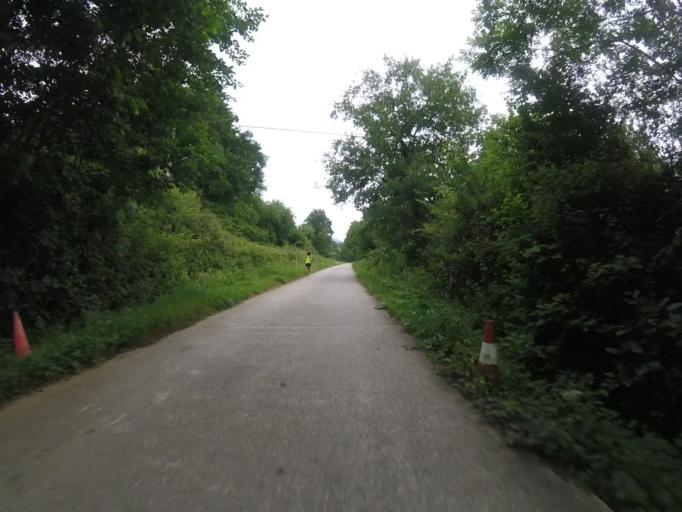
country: ES
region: Navarre
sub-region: Provincia de Navarra
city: Sunbilla
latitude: 43.1576
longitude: -1.6717
